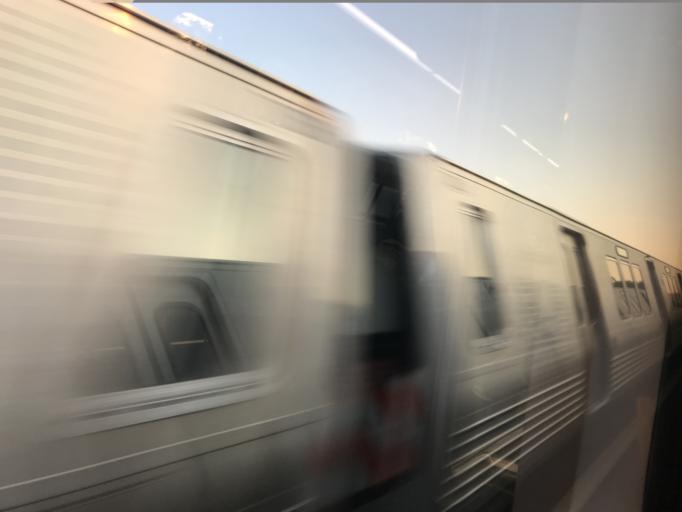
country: US
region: Maryland
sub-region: Prince George's County
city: College Park
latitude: 38.9874
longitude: -76.9246
